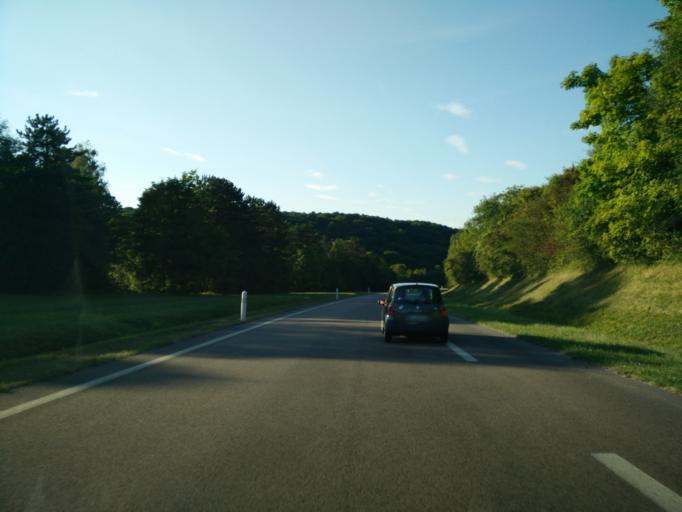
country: FR
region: Ile-de-France
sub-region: Departement des Yvelines
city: Bonnieres-sur-Seine
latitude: 49.0161
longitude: 1.5882
